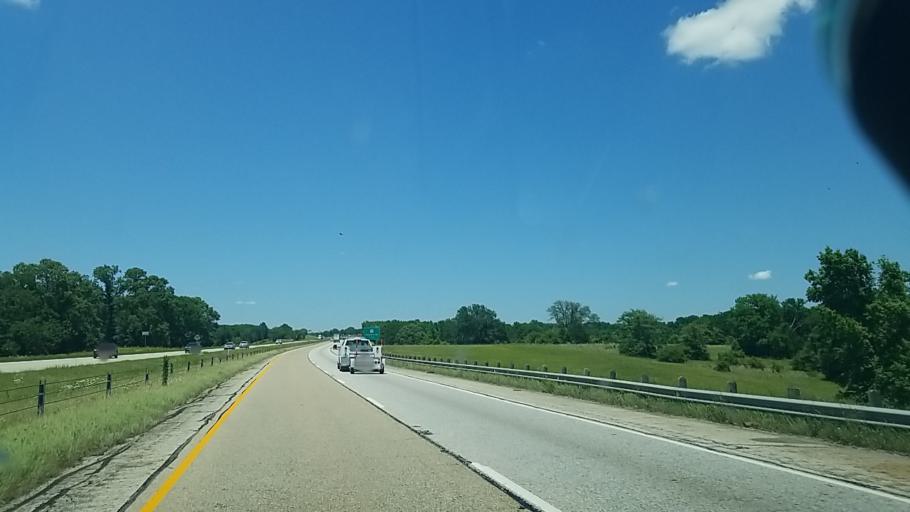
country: US
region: Texas
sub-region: Leon County
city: Centerville
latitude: 31.2388
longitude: -95.9925
